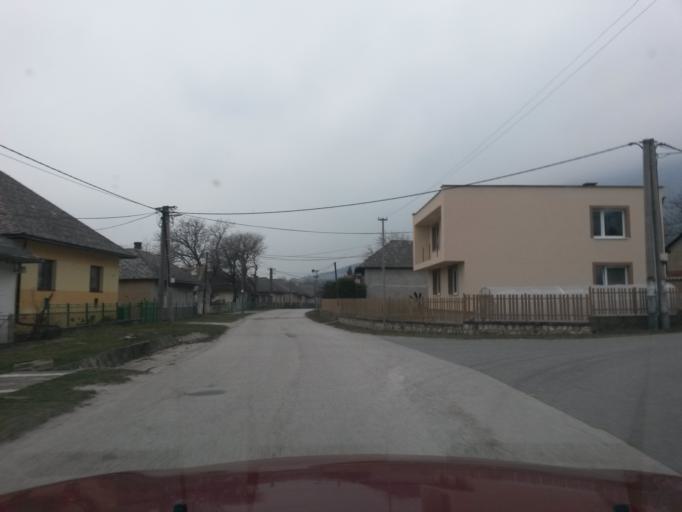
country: SK
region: Kosicky
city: Medzev
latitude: 48.6053
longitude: 20.7546
